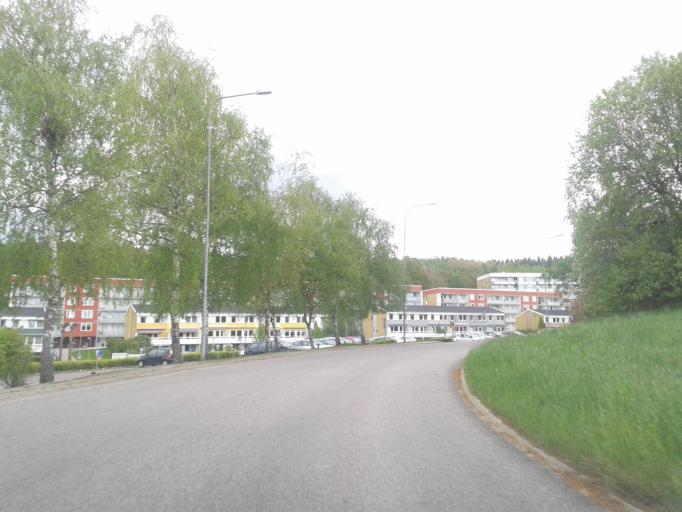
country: SE
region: Vaestra Goetaland
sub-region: Kungalvs Kommun
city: Kungalv
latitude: 57.8786
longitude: 11.9932
